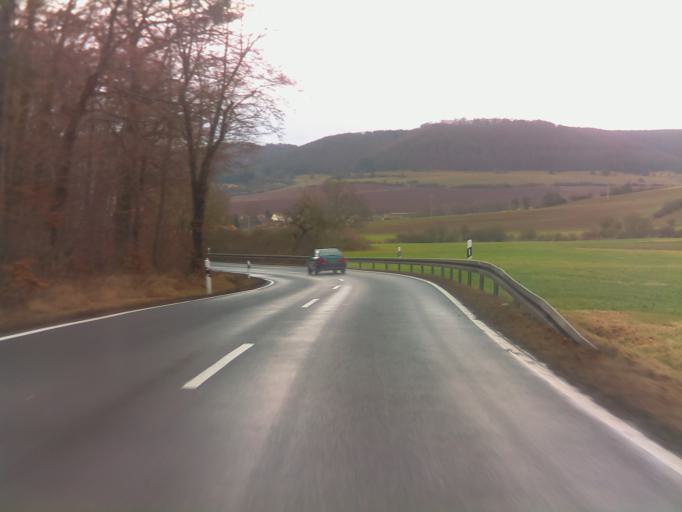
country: DE
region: Thuringia
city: Stepfershausen
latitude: 50.5837
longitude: 10.3234
